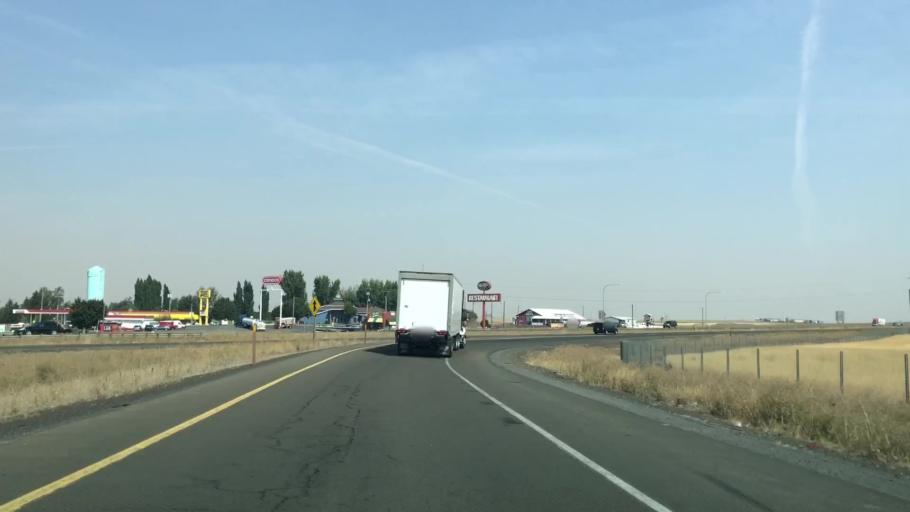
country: US
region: Washington
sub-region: Adams County
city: Ritzville
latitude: 47.1165
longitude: -118.3644
